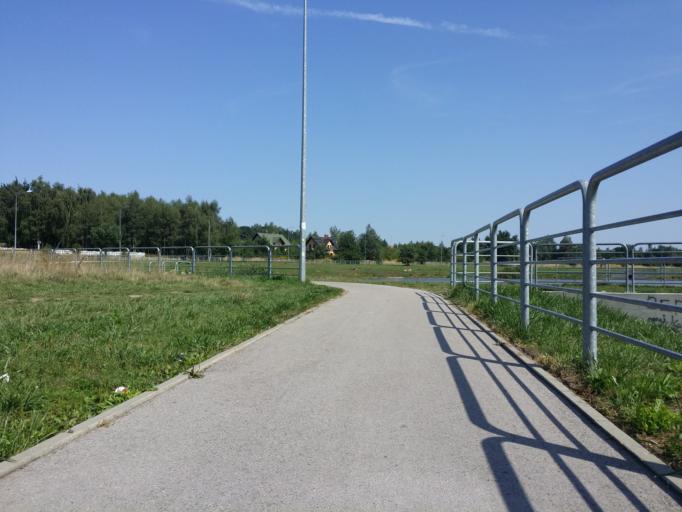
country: PL
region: Masovian Voivodeship
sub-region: Powiat radomski
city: Trablice
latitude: 51.3684
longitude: 21.1391
